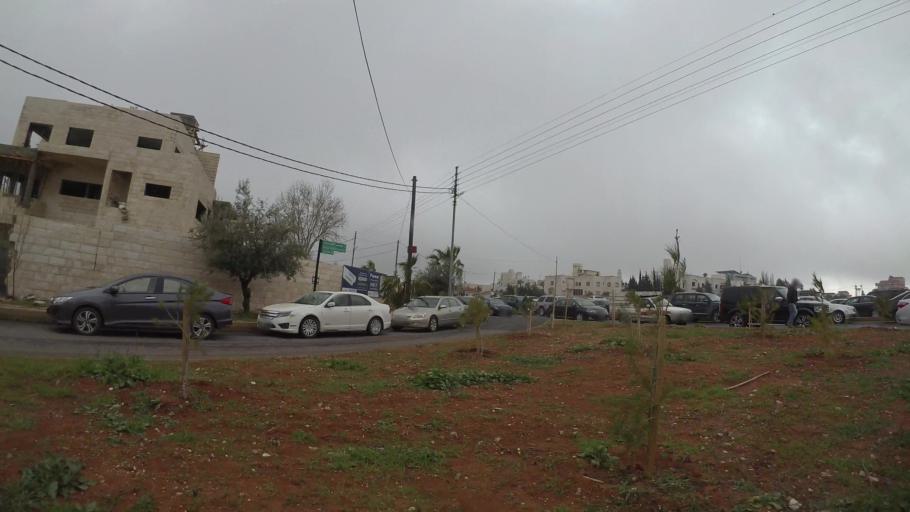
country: JO
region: Amman
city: Al Bunayyat ash Shamaliyah
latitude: 31.9403
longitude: 35.8777
